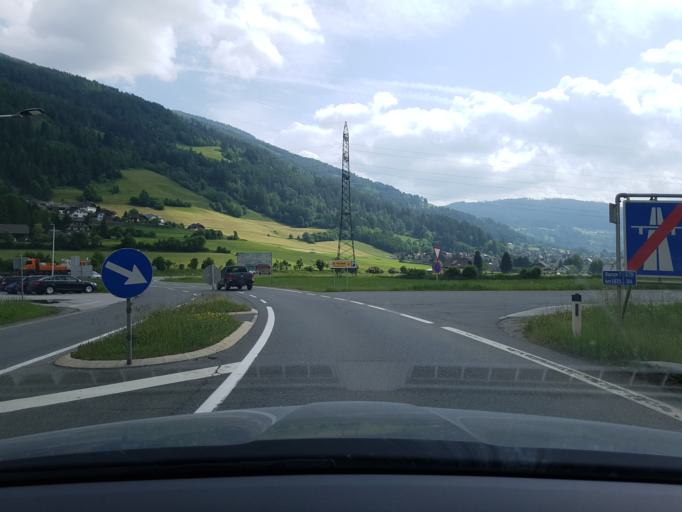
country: AT
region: Salzburg
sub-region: Politischer Bezirk Tamsweg
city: Sankt Michael im Lungau
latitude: 47.0961
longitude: 13.6171
